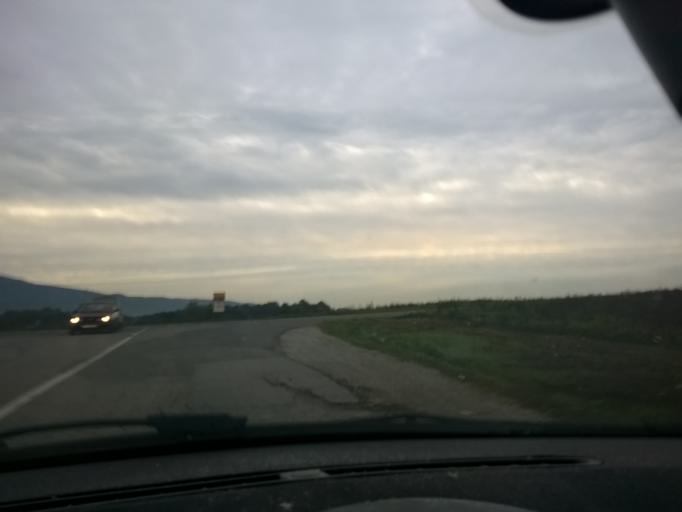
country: HR
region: Zagrebacka
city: Pojatno
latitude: 45.9111
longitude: 15.8180
